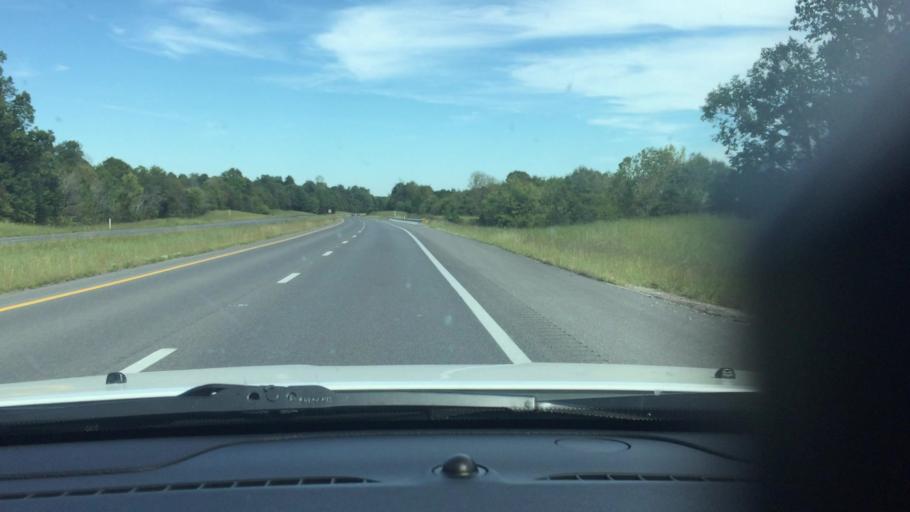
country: US
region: Kentucky
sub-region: Caldwell County
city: Princeton
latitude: 37.1151
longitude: -87.9275
